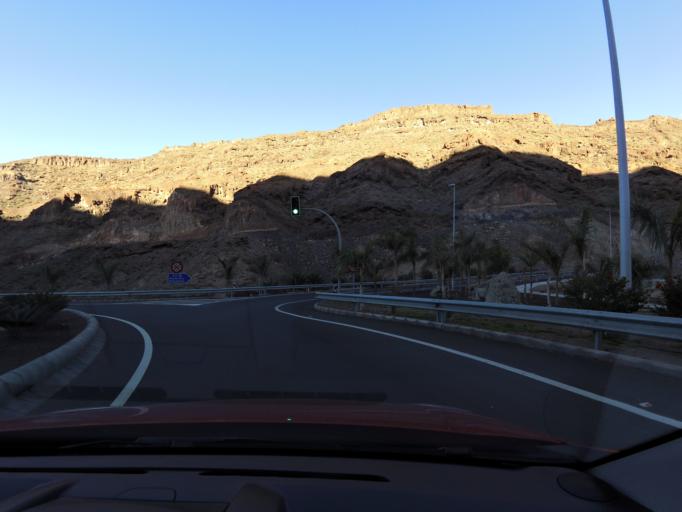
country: ES
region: Canary Islands
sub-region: Provincia de Las Palmas
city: Puerto Rico
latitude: 27.8239
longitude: -15.7475
